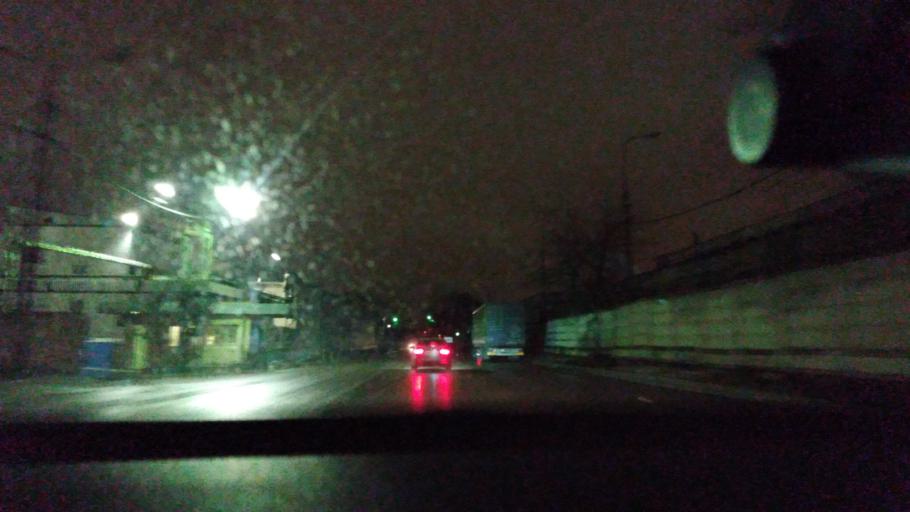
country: RU
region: Moskovskaya
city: Reutov
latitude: 55.7724
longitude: 37.8722
